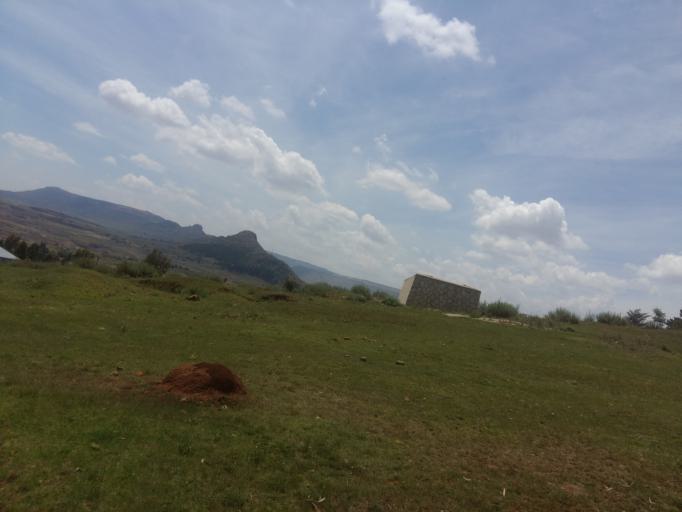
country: LS
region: Mafeteng
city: Mafeteng
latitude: -29.7036
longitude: 27.4353
